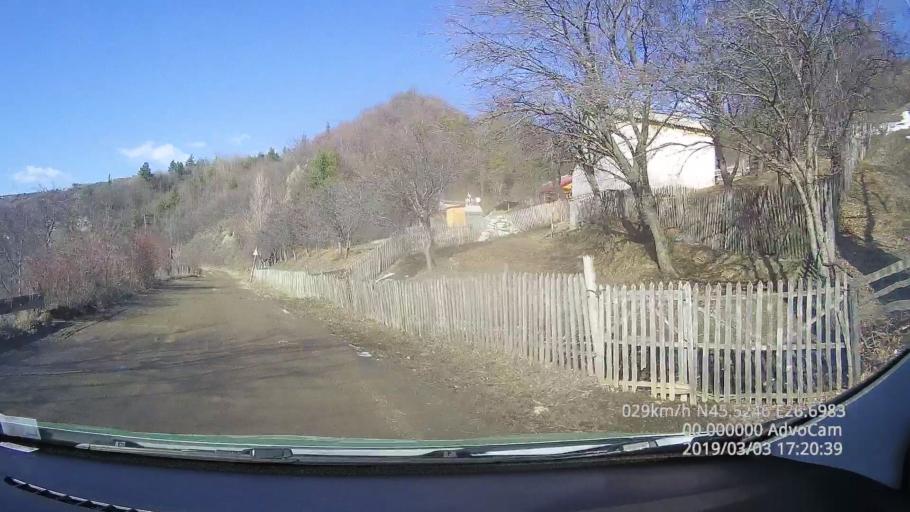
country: RO
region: Buzau
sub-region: Comuna Bisoca
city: Bisoca
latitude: 45.5248
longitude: 26.6984
